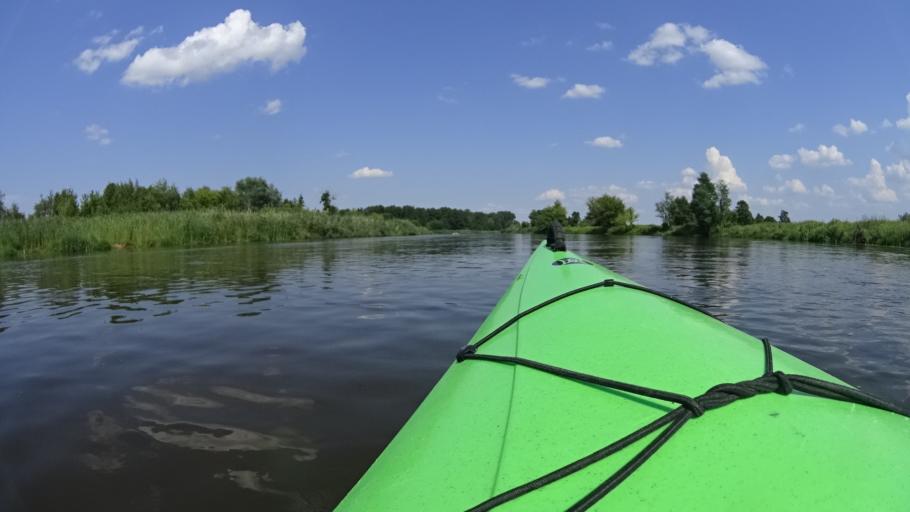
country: PL
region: Masovian Voivodeship
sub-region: Powiat bialobrzeski
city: Wysmierzyce
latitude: 51.6555
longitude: 20.8447
